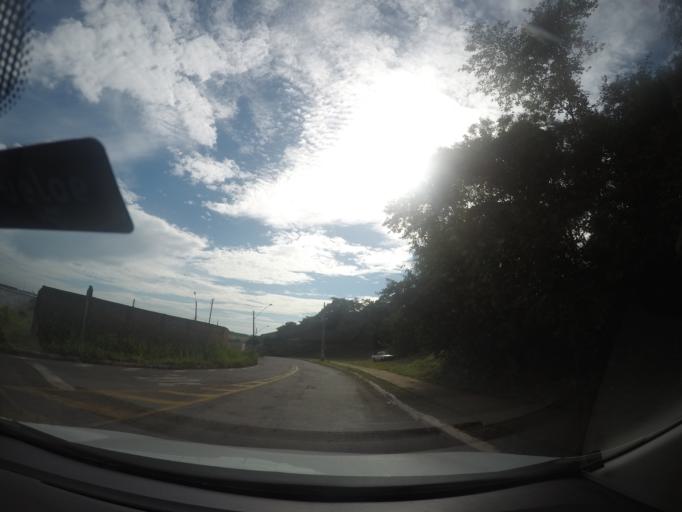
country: BR
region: Goias
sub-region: Goiania
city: Goiania
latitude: -16.6869
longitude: -49.2029
